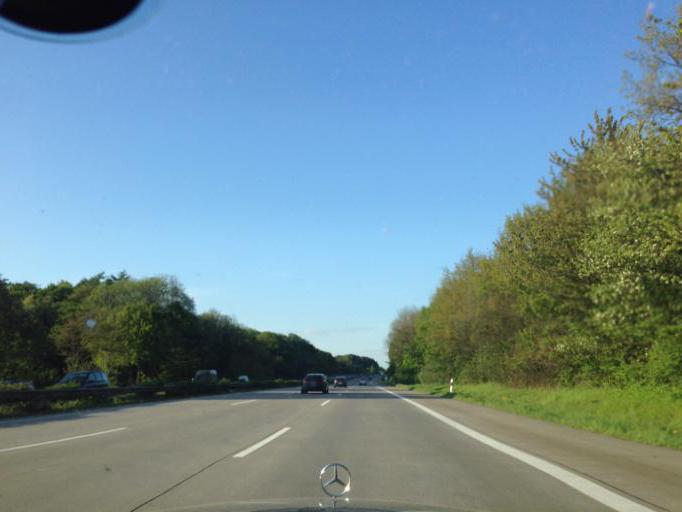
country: DE
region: Schleswig-Holstein
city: Lasbek
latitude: 53.7450
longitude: 10.3622
